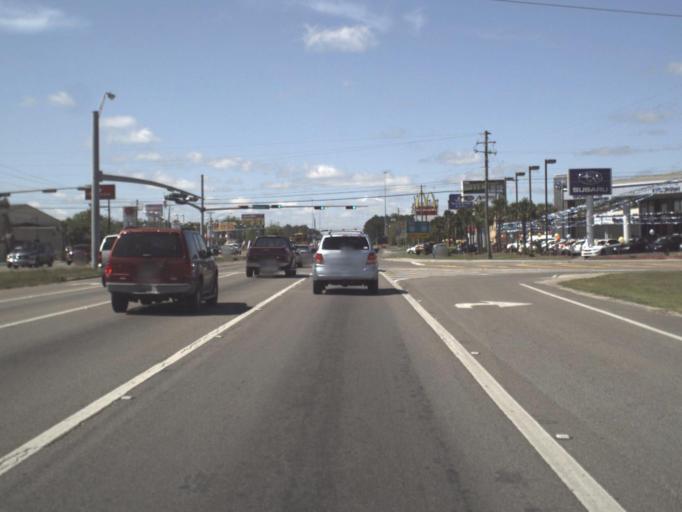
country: US
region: Florida
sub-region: Escambia County
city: Ensley
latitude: 30.4938
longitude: -87.2618
